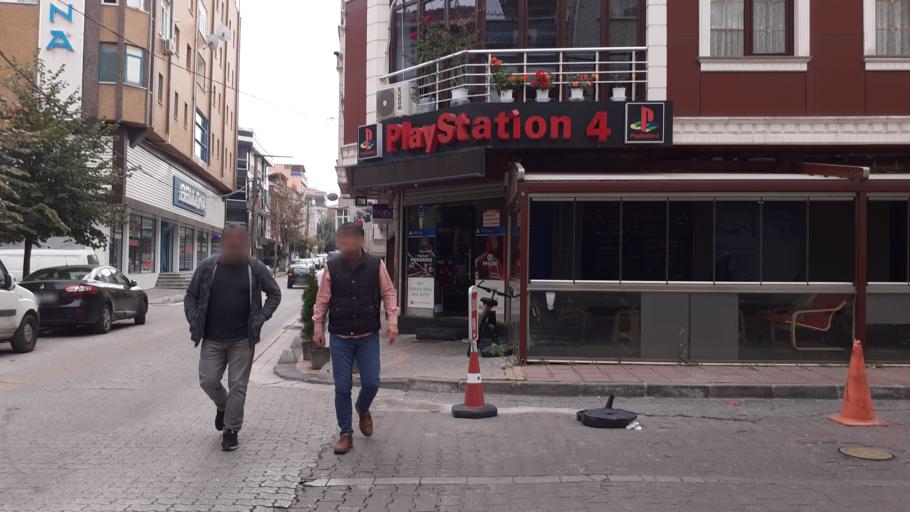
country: TR
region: Istanbul
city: Mahmutbey
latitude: 40.9923
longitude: 28.7853
